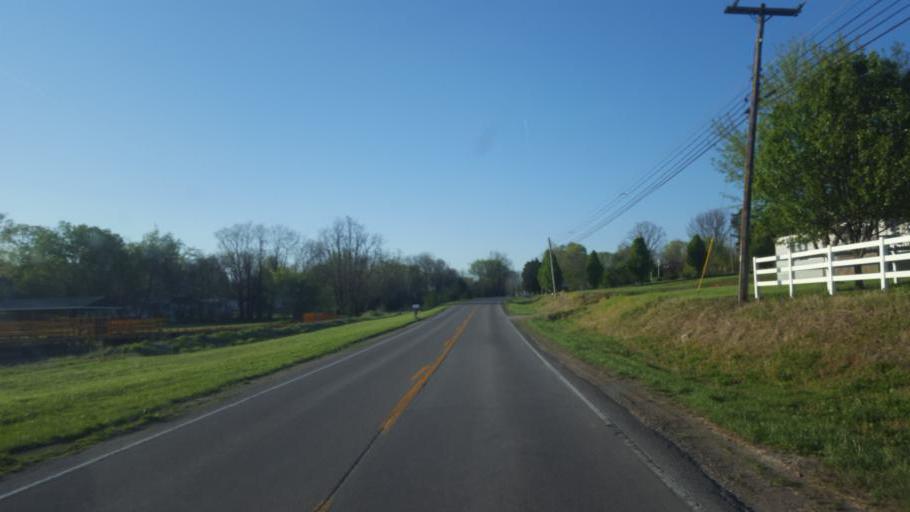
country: US
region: Kentucky
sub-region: Hart County
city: Munfordville
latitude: 37.2392
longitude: -85.8923
